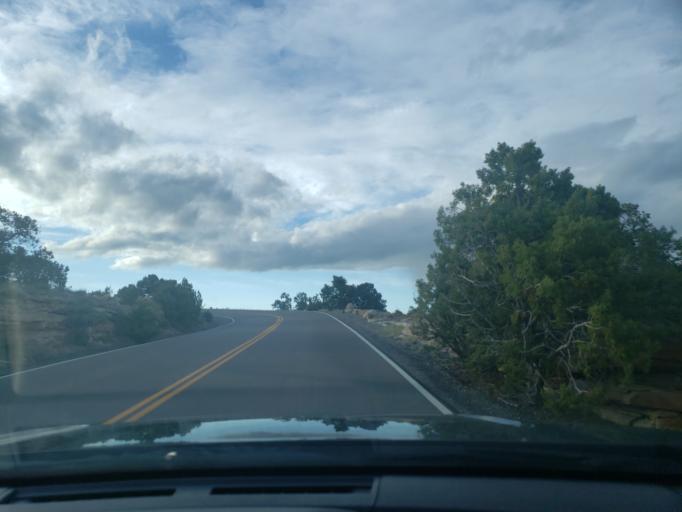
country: US
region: Colorado
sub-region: Mesa County
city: Redlands
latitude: 39.0328
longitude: -108.6494
